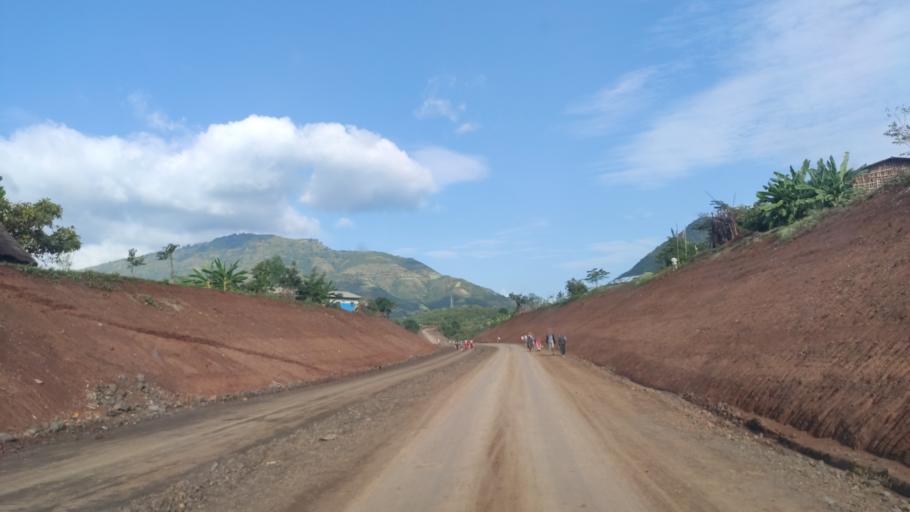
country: ET
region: Southern Nations, Nationalities, and People's Region
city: Arba Minch'
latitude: 6.4264
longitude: 37.3212
